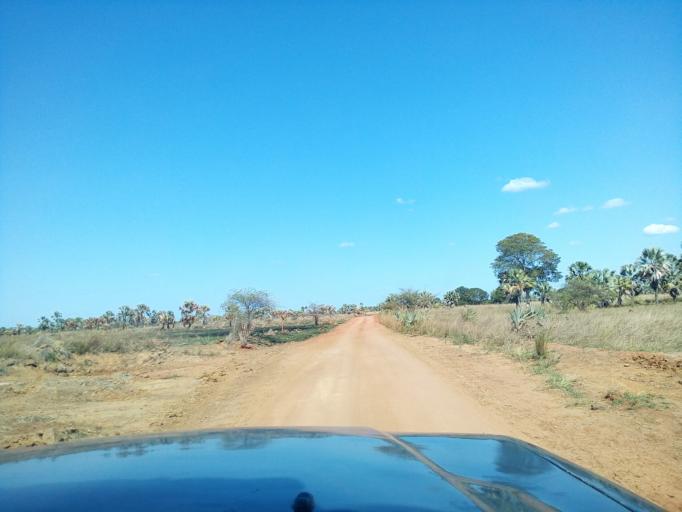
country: MG
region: Boeny
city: Mahajanga
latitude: -15.8575
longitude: 46.1504
